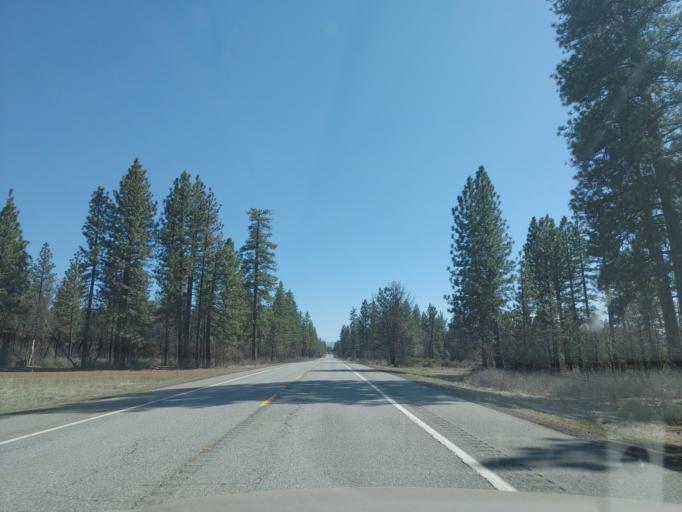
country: US
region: California
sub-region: Shasta County
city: Burney
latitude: 40.9516
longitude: -121.6119
